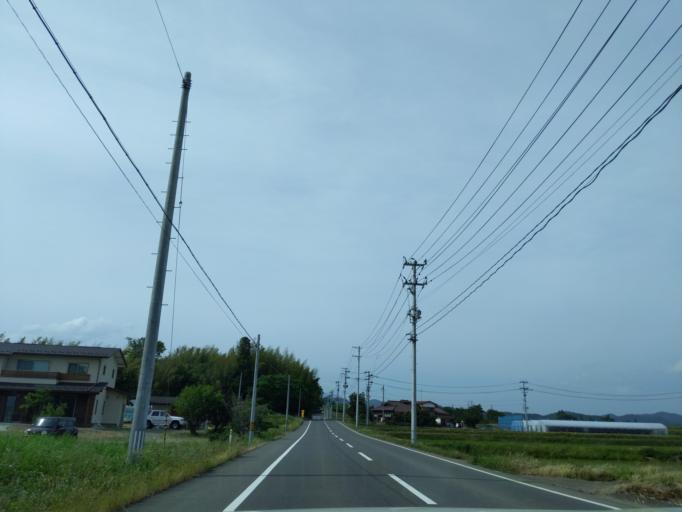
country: JP
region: Fukushima
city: Koriyama
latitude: 37.4570
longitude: 140.3127
